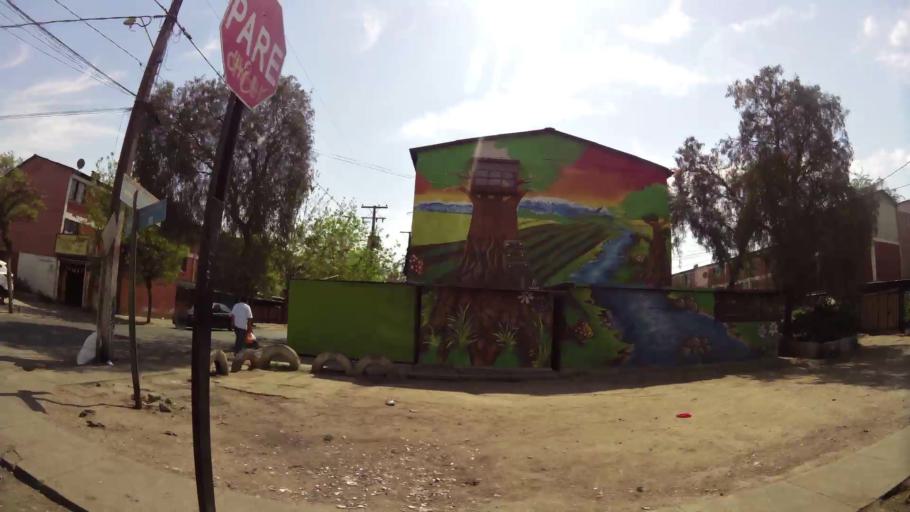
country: CL
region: Santiago Metropolitan
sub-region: Provincia de Santiago
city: La Pintana
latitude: -33.5589
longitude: -70.6343
